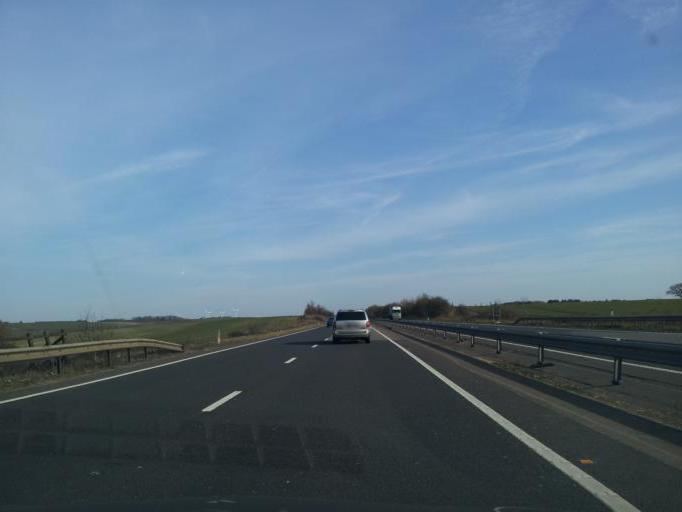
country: GB
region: England
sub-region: Bedford
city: Pertenhall
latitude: 52.3505
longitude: -0.3697
